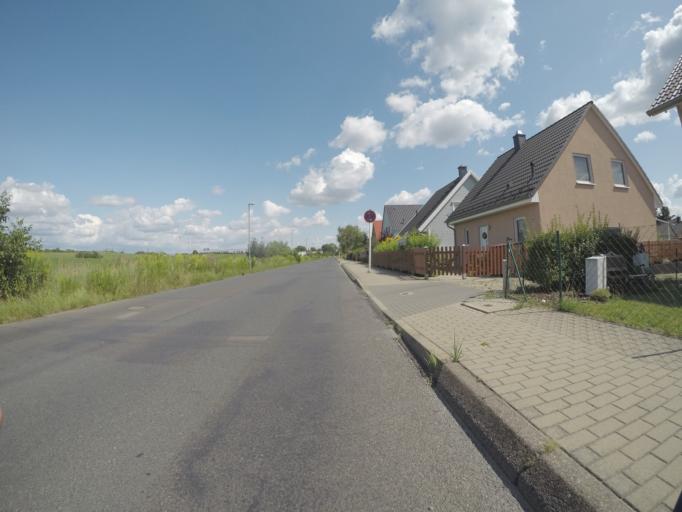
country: DE
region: Berlin
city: Mahlsdorf
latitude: 52.5021
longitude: 13.5991
